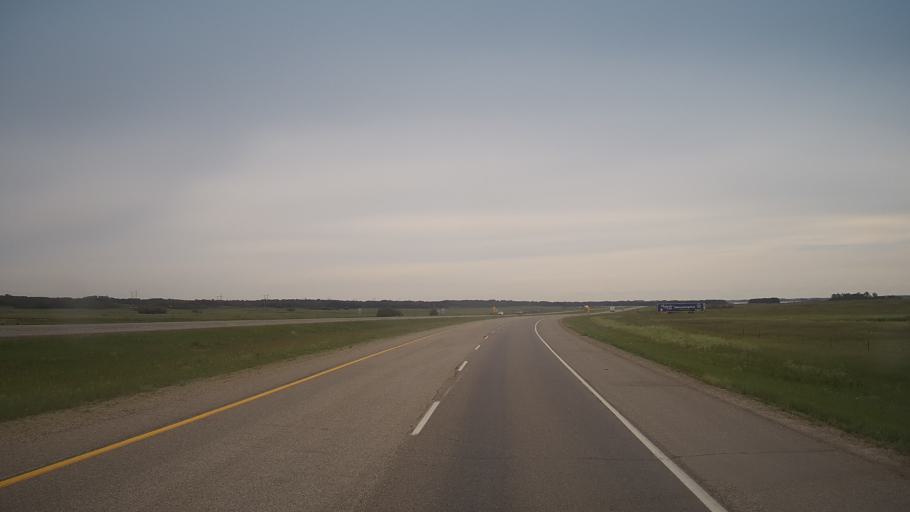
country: CA
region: Saskatchewan
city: Saskatoon
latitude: 51.8545
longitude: -106.5070
